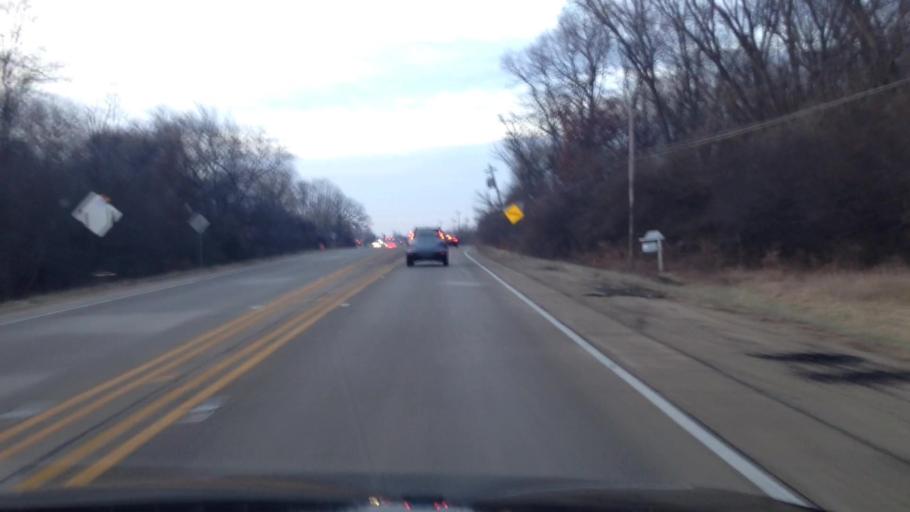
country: US
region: Illinois
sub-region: Kane County
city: Carpentersville
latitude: 42.1491
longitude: -88.2539
